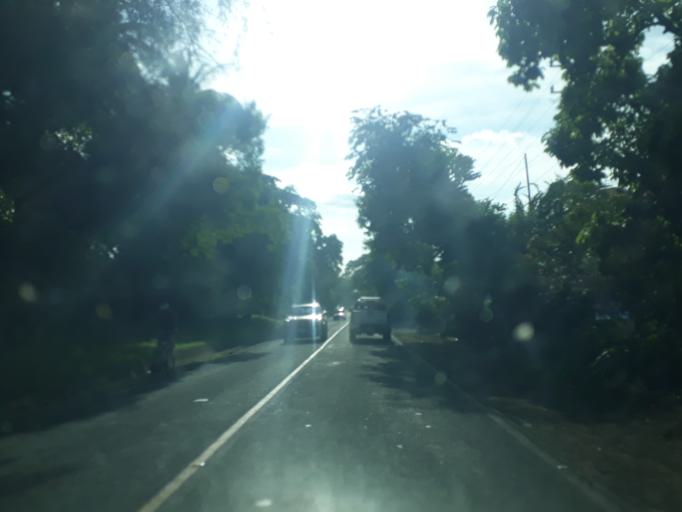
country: NI
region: Masaya
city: Masatepe
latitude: 11.9052
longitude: -86.1703
